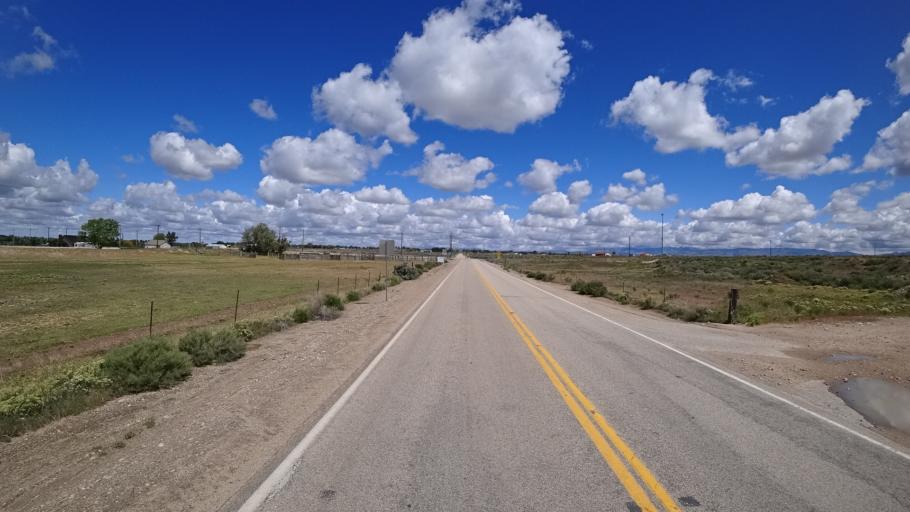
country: US
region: Idaho
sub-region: Ada County
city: Kuna
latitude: 43.5159
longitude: -116.3146
